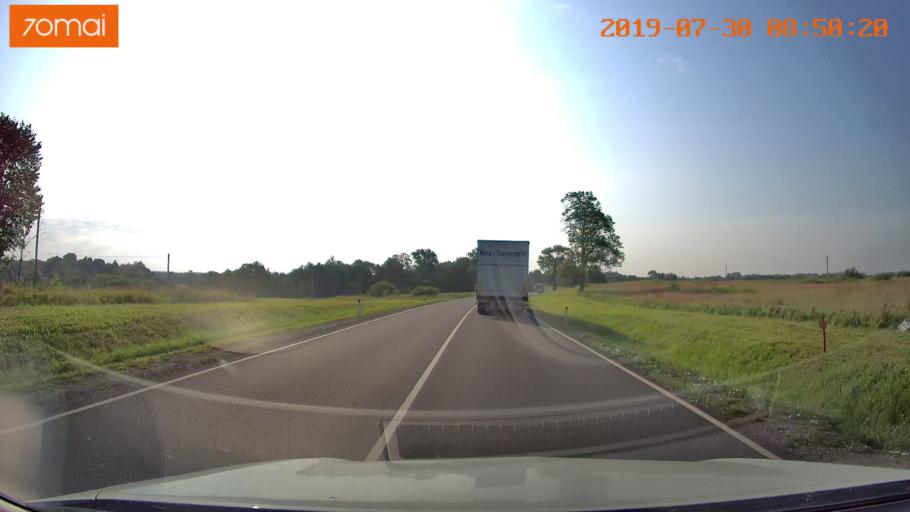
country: RU
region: Kaliningrad
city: Chernyakhovsk
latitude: 54.6081
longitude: 21.9375
